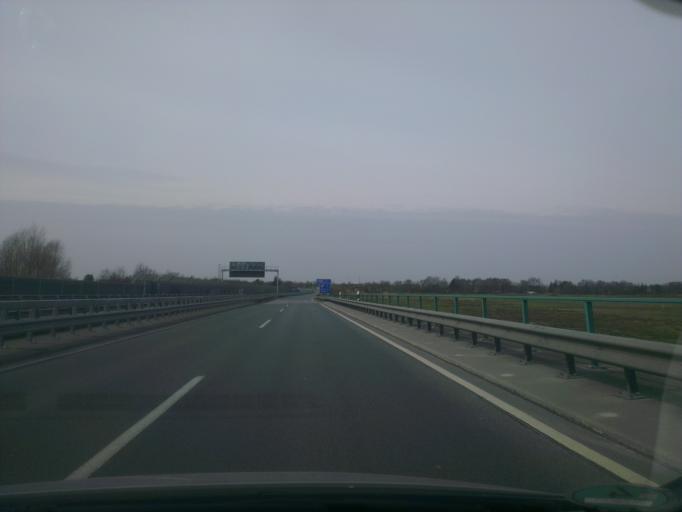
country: DE
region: Lower Saxony
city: Emden
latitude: 53.3874
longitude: 7.1966
